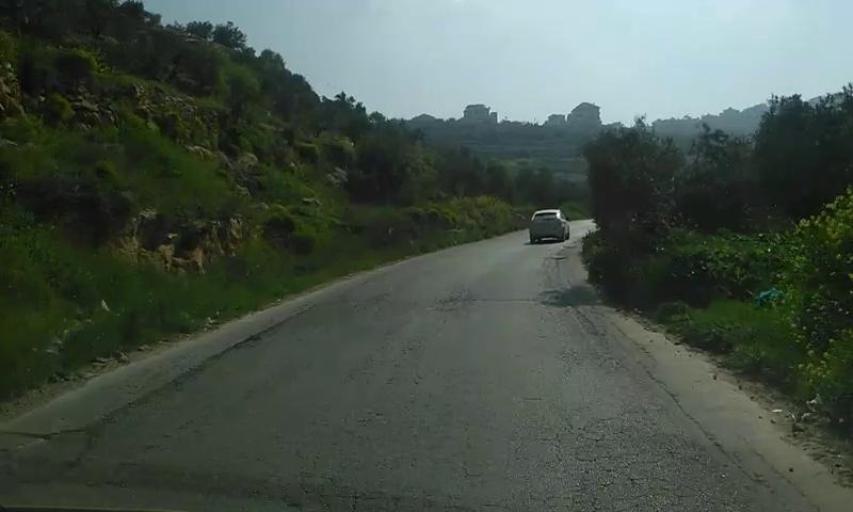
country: PS
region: West Bank
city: `Ayn Yabrud
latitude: 31.9515
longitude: 35.2416
